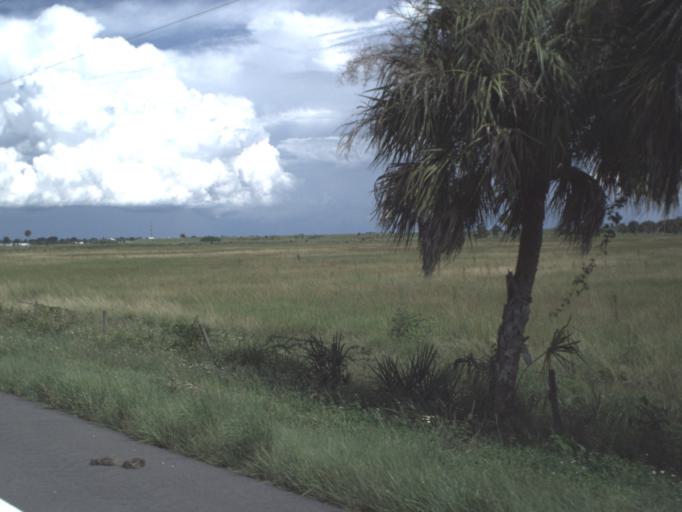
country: US
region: Florida
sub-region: Glades County
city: Buckhead Ridge
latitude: 27.1205
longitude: -80.9206
